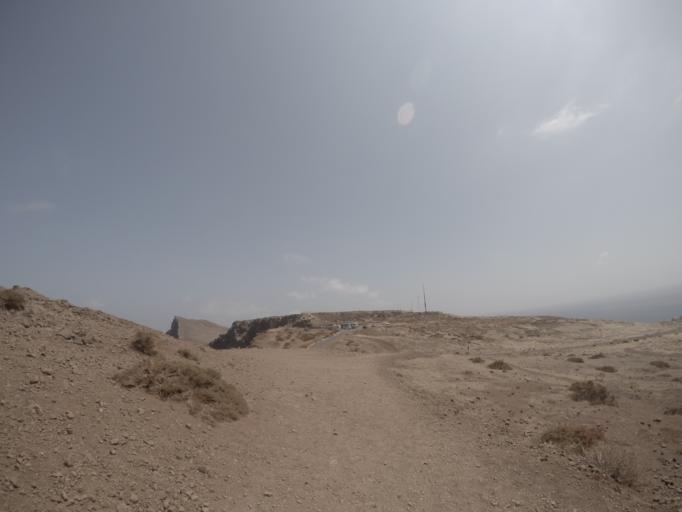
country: PT
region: Madeira
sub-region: Machico
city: Canical
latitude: 32.7503
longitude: -16.7076
